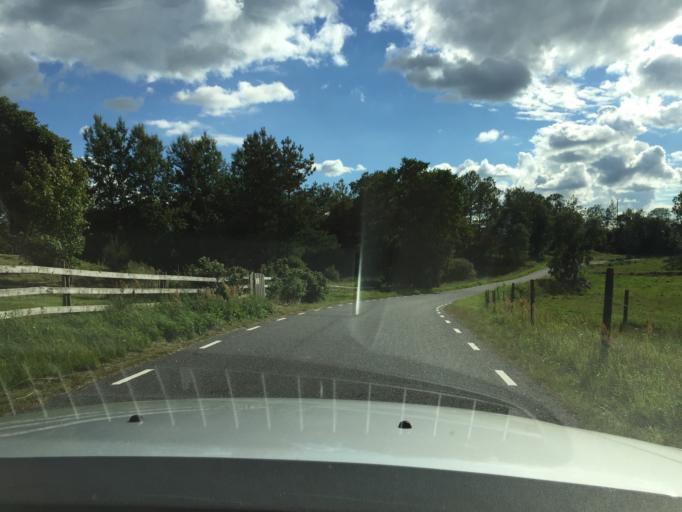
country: SE
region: Skane
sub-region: Hassleholms Kommun
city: Sosdala
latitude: 56.0023
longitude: 13.7800
